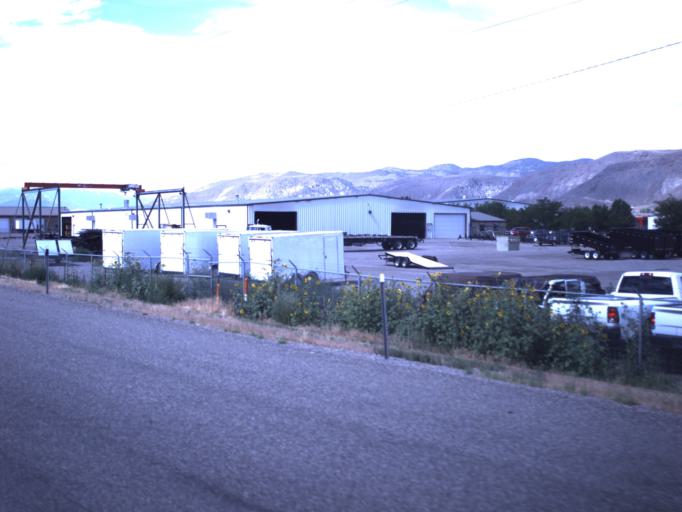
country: US
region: Utah
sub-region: Sevier County
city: Richfield
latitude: 38.7368
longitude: -112.0941
